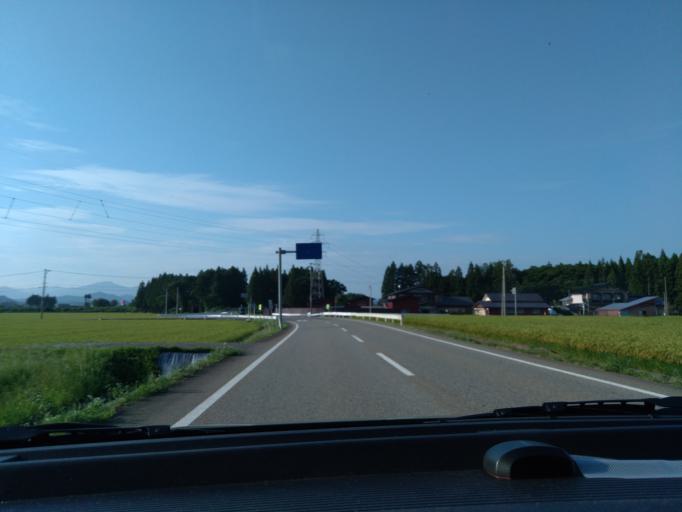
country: JP
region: Akita
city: Kakunodatemachi
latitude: 39.5379
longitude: 140.5581
